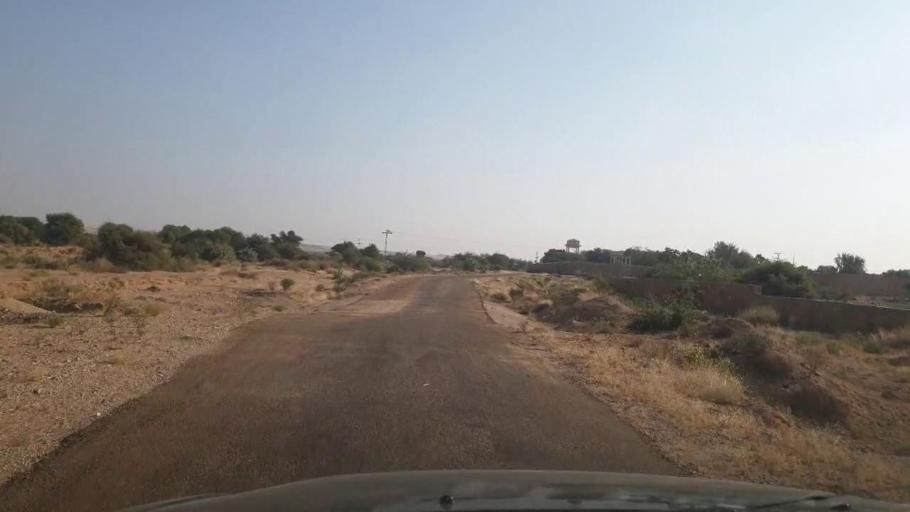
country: PK
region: Sindh
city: Jamshoro
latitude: 25.3311
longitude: 67.8448
